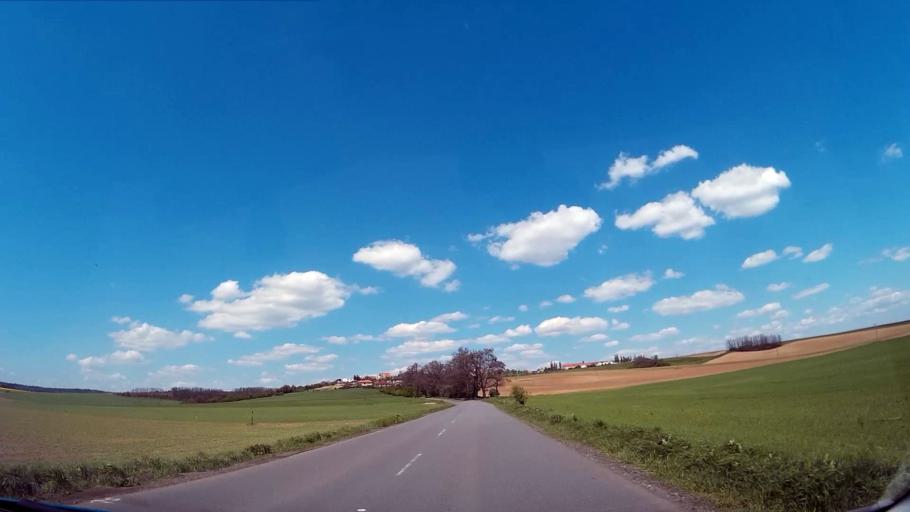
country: CZ
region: South Moravian
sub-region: Okres Brno-Venkov
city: Rosice
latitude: 49.1496
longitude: 16.3833
